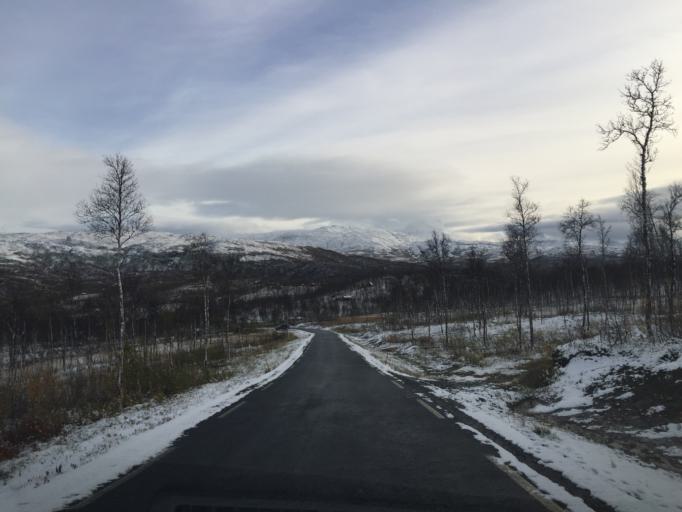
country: NO
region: Nordland
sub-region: Sorfold
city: Straumen
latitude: 67.0866
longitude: 16.0217
